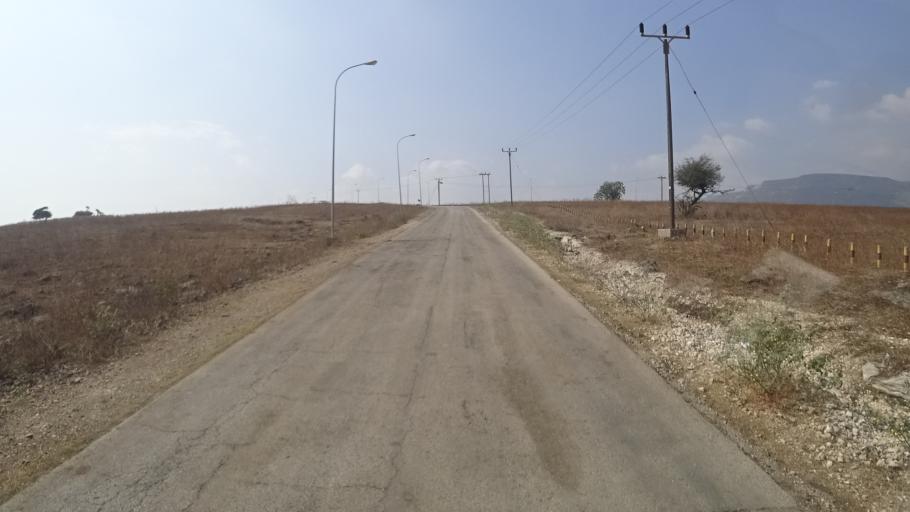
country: YE
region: Al Mahrah
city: Hawf
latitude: 16.7307
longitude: 53.2661
